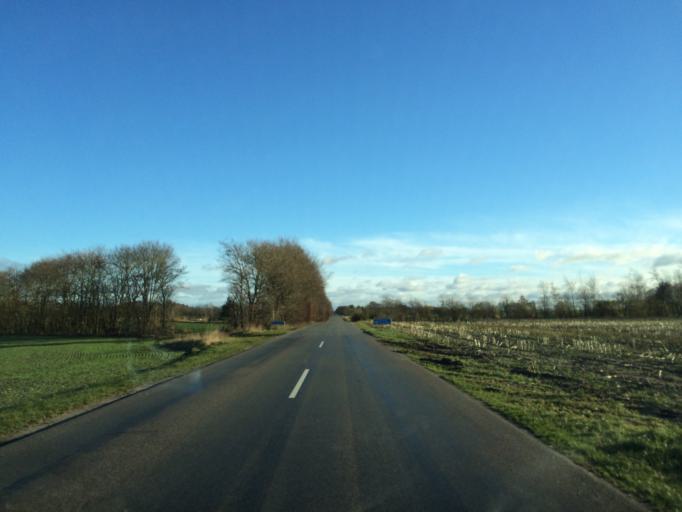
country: DK
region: Central Jutland
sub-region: Herning Kommune
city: Kibaek
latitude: 56.0517
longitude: 8.7924
